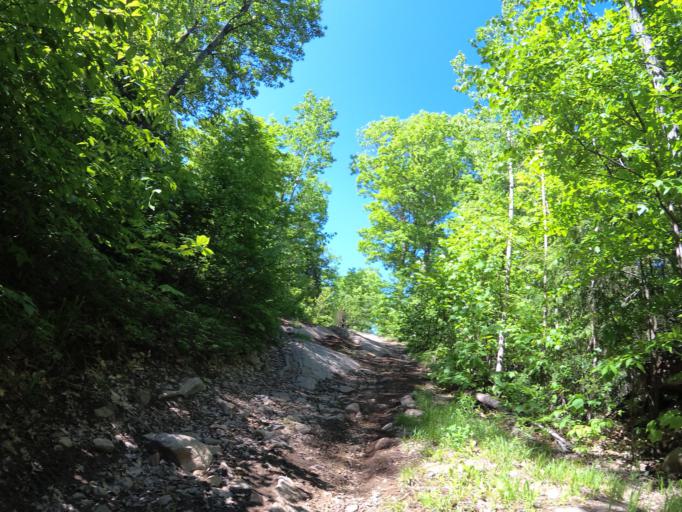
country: CA
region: Ontario
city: Renfrew
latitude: 45.0637
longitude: -77.0778
